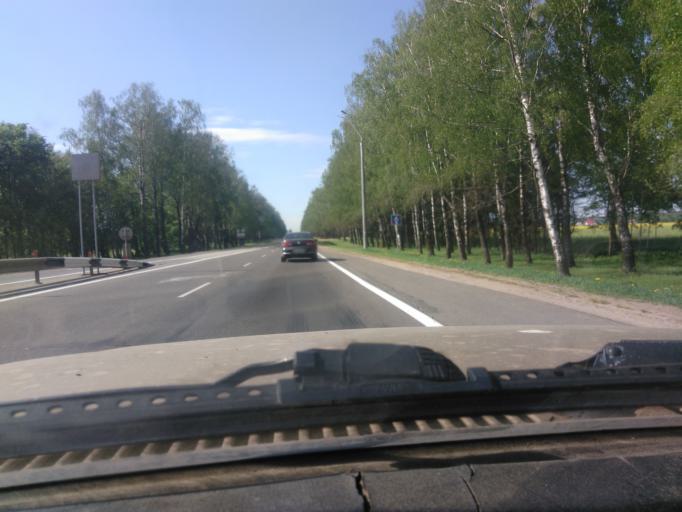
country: BY
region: Mogilev
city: Buynichy
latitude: 53.8483
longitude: 30.2519
